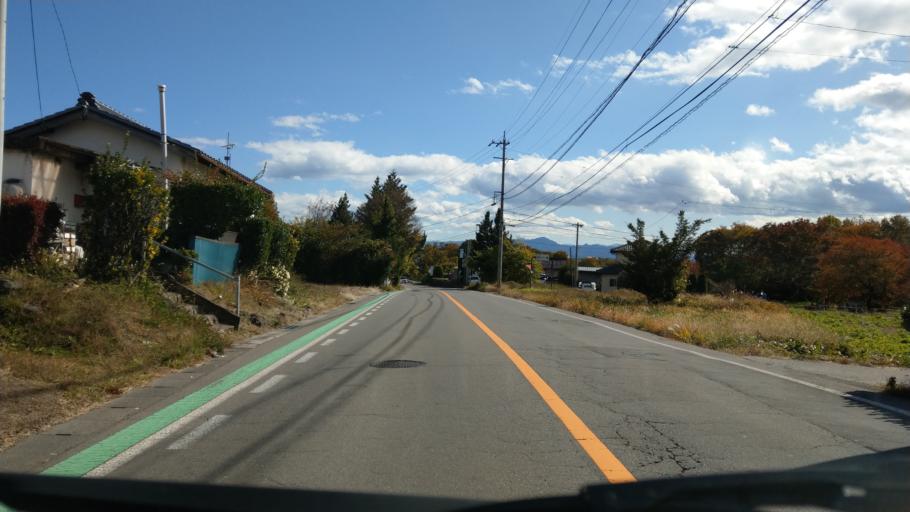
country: JP
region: Nagano
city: Komoro
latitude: 36.3090
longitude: 138.4275
